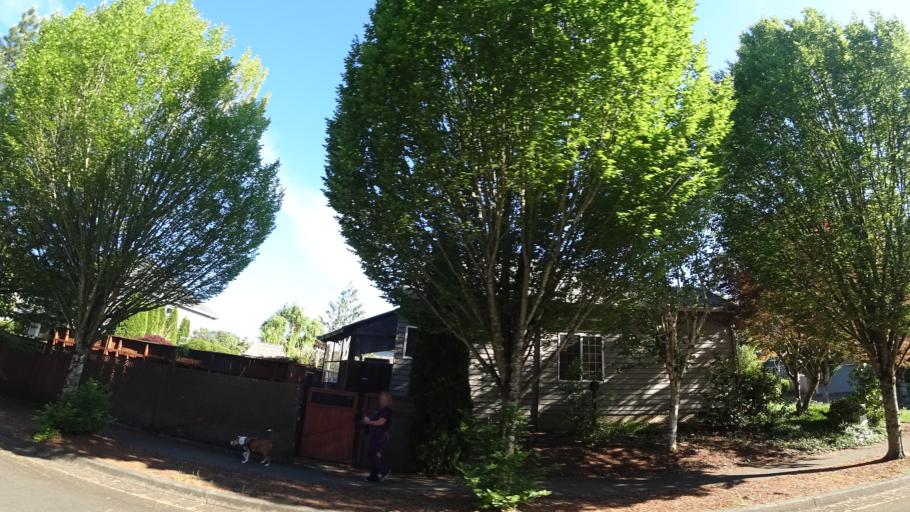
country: US
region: Oregon
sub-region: Washington County
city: Beaverton
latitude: 45.4616
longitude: -122.8113
